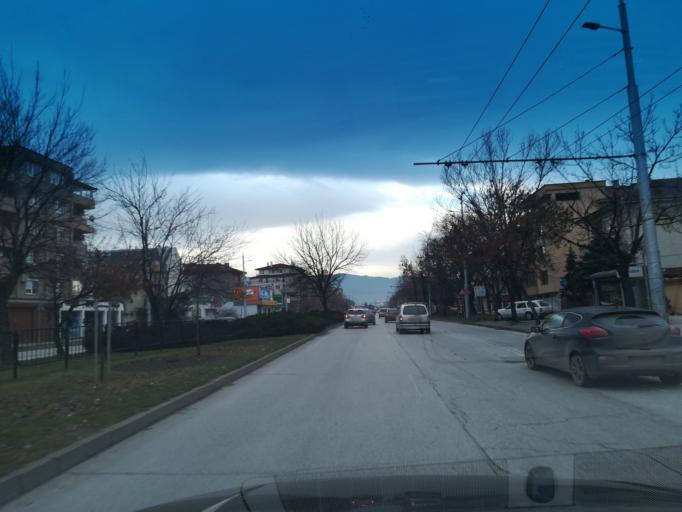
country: BG
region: Plovdiv
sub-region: Obshtina Plovdiv
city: Plovdiv
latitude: 42.1289
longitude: 24.7225
